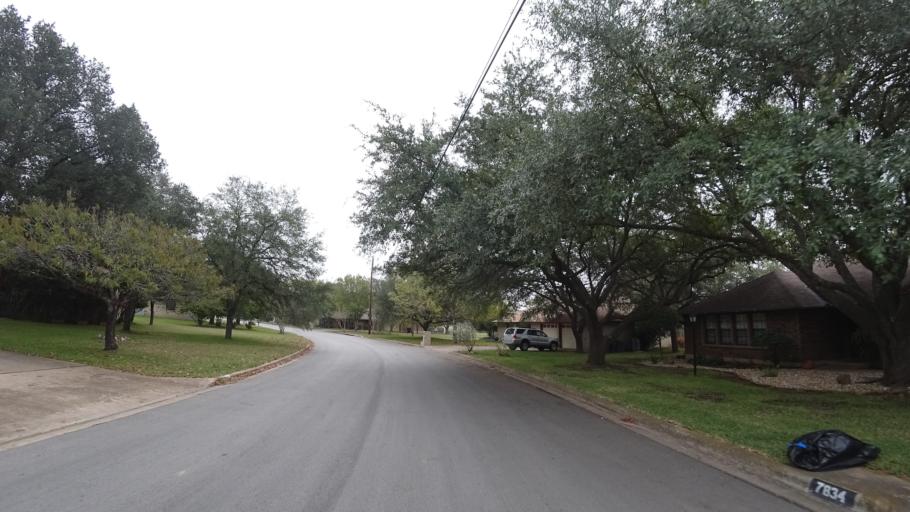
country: US
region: Texas
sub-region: Travis County
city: Shady Hollow
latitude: 30.2138
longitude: -97.9071
